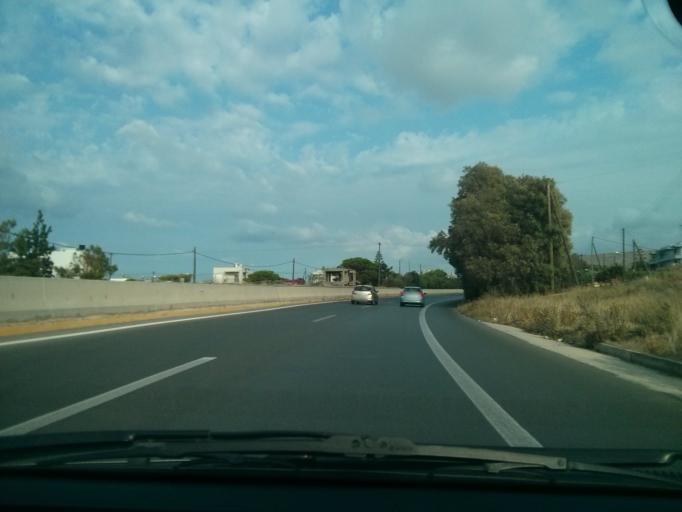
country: GR
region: Crete
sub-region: Nomos Irakleiou
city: Kokkini Hani
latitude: 35.3304
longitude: 25.2436
